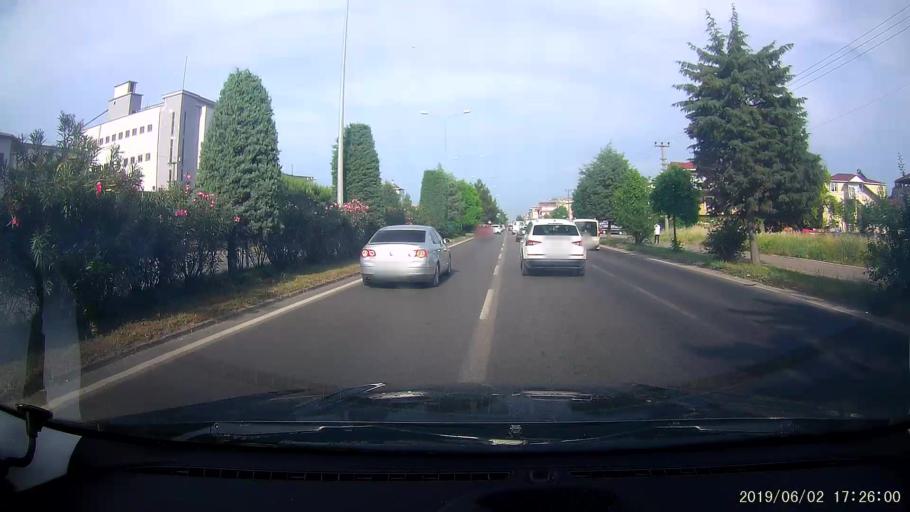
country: TR
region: Samsun
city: Carsamba
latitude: 41.2045
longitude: 36.7143
